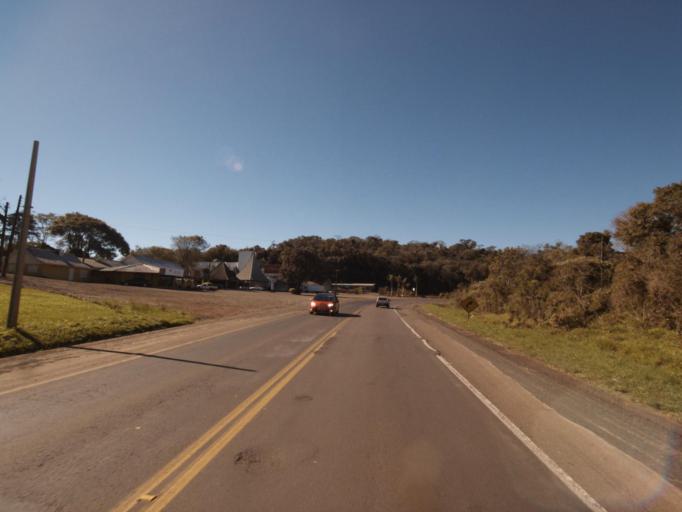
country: BR
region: Santa Catarina
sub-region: Chapeco
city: Chapeco
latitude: -26.9651
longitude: -52.5660
